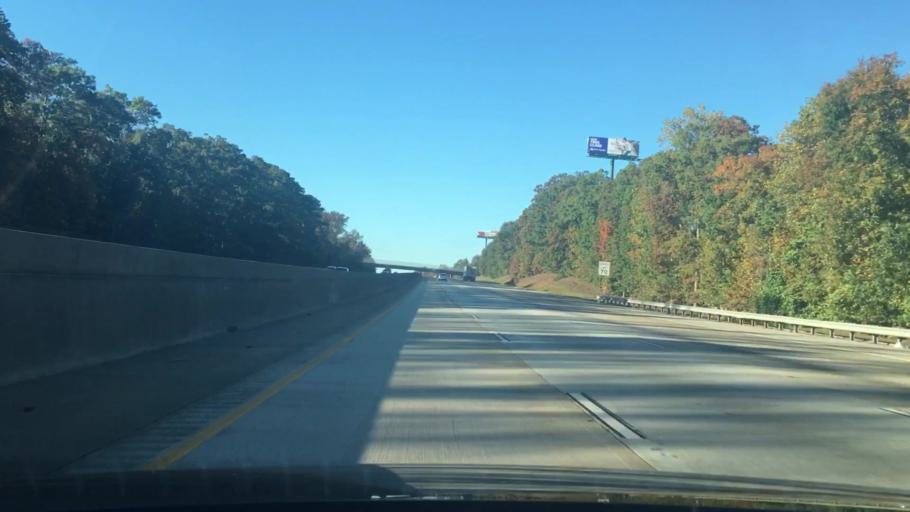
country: US
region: Georgia
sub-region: Fulton County
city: Palmetto
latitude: 33.5234
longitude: -84.6199
